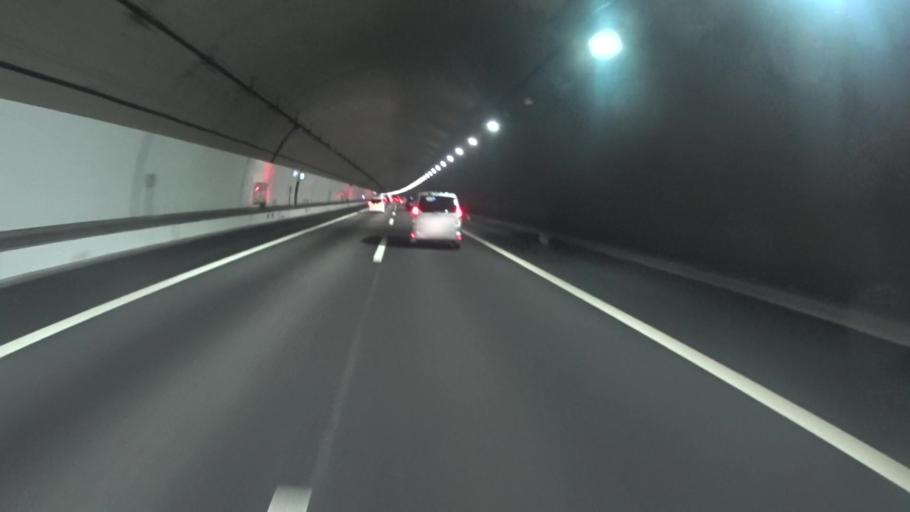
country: JP
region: Shiga Prefecture
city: Minakuchicho-matoba
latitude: 34.9222
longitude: 136.1216
